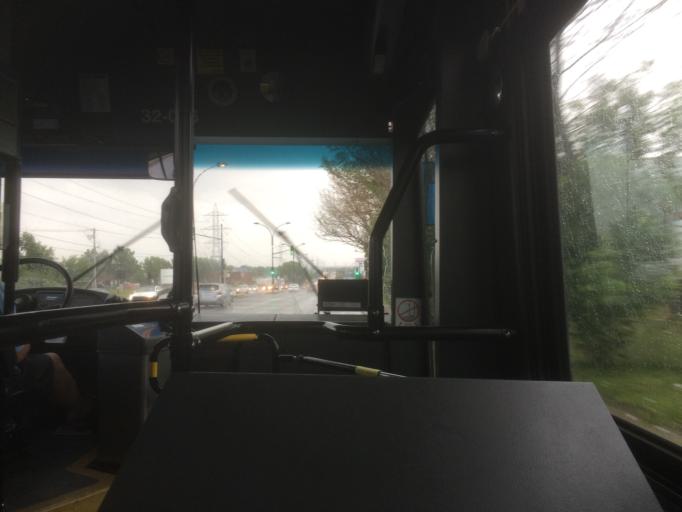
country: CA
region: Quebec
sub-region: Montreal
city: Saint-Leonard
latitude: 45.6242
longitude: -73.5836
